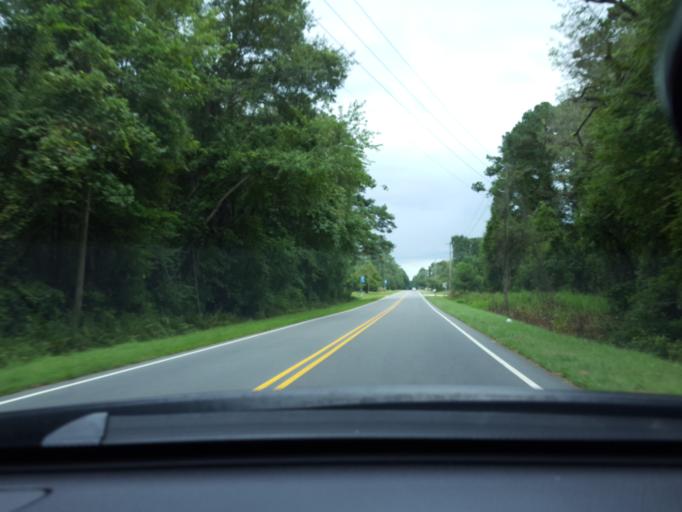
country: US
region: North Carolina
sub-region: Sampson County
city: Roseboro
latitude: 34.7818
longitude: -78.3983
